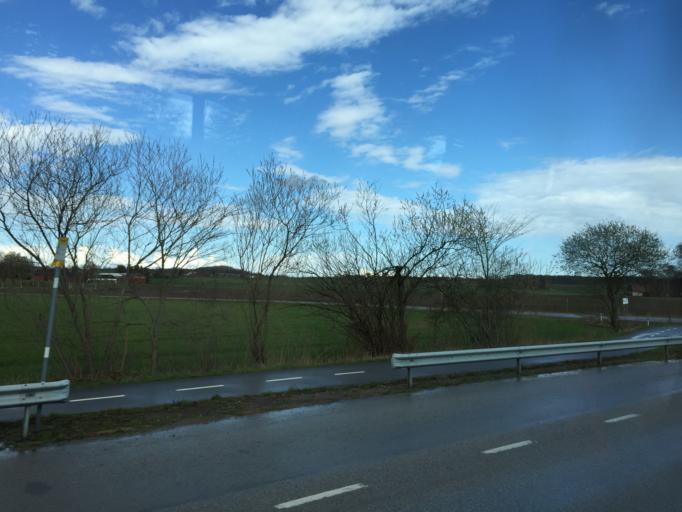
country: SE
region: Skane
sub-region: Staffanstorps Kommun
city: Staffanstorp
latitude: 55.6779
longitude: 13.2890
